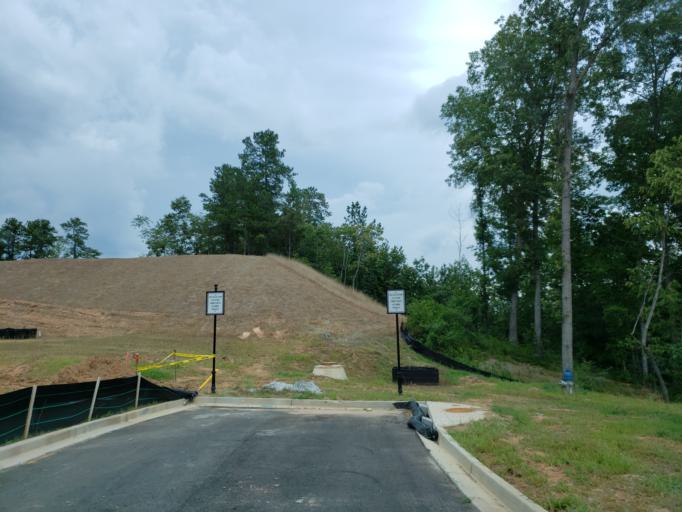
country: US
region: Georgia
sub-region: Cherokee County
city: Woodstock
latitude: 34.1156
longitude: -84.5266
